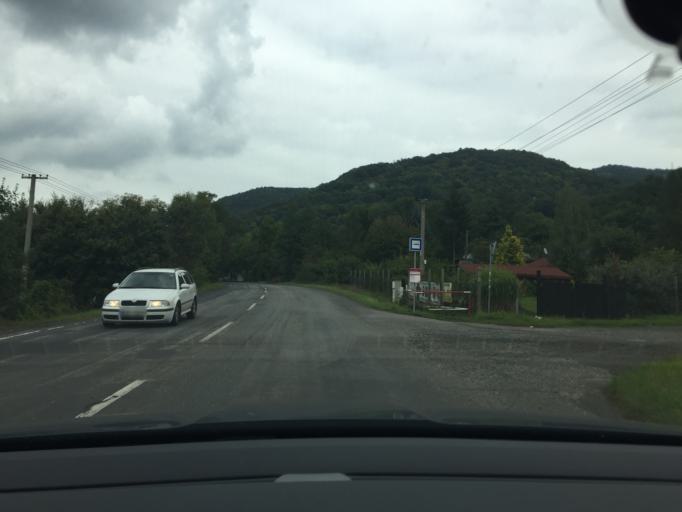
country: CZ
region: Ustecky
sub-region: Okres Usti nad Labem
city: Usti nad Labem
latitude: 50.5974
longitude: 14.0715
